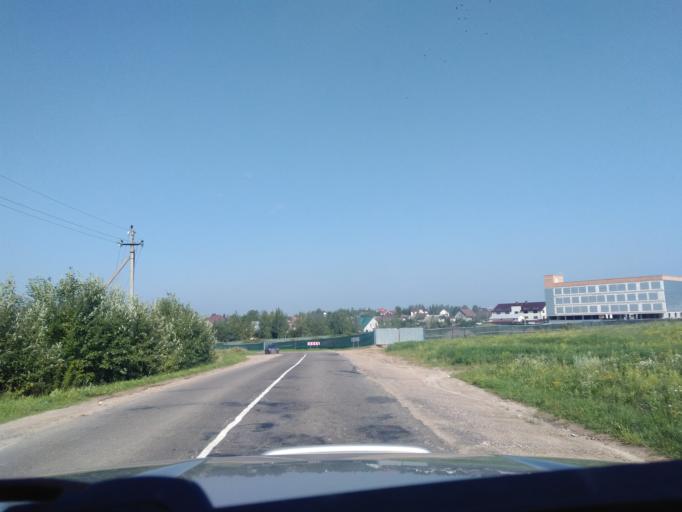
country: BY
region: Minsk
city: Zhdanovichy
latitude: 53.9318
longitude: 27.4163
